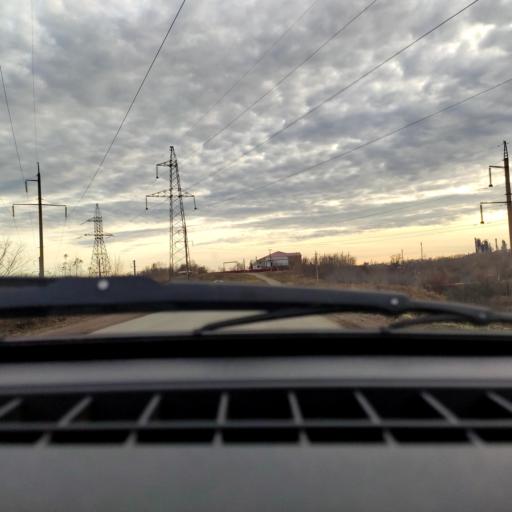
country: RU
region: Bashkortostan
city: Ufa
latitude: 54.8663
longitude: 56.1284
